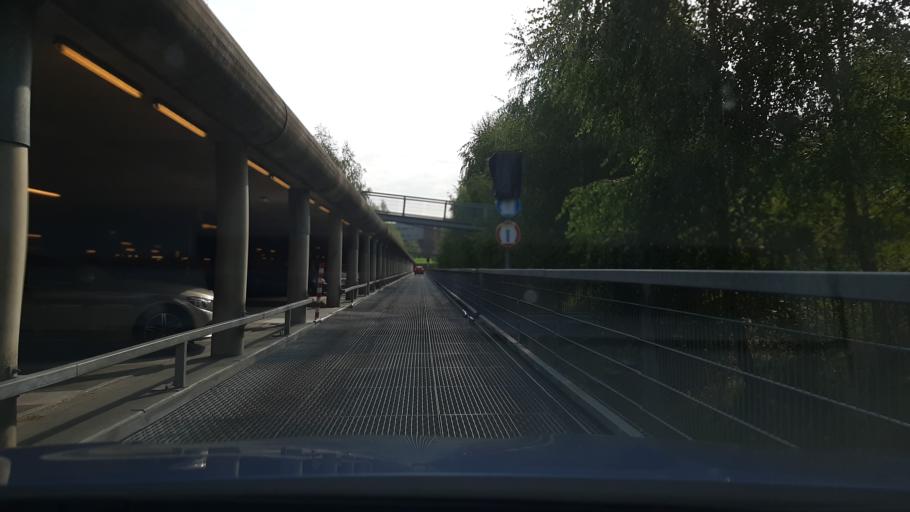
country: NL
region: Limburg
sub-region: Gemeente Sittard-Geleen
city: Limbricht
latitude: 50.9839
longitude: 5.8394
